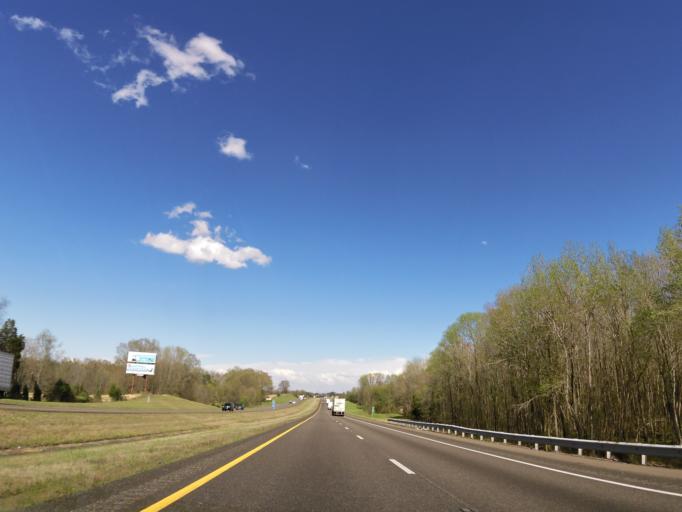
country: US
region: Tennessee
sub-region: Henderson County
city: Lexington
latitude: 35.7834
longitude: -88.4095
